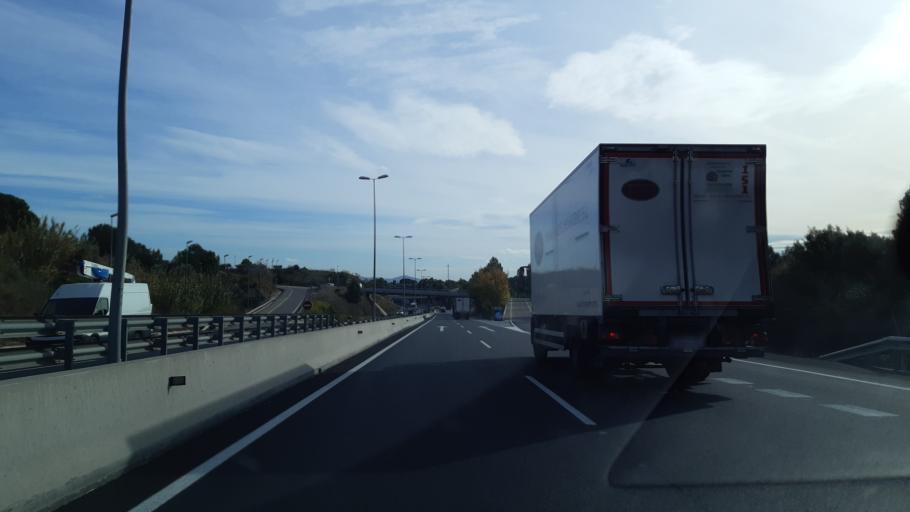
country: ES
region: Catalonia
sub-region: Provincia de Barcelona
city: Esparreguera
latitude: 41.5349
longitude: 1.8623
